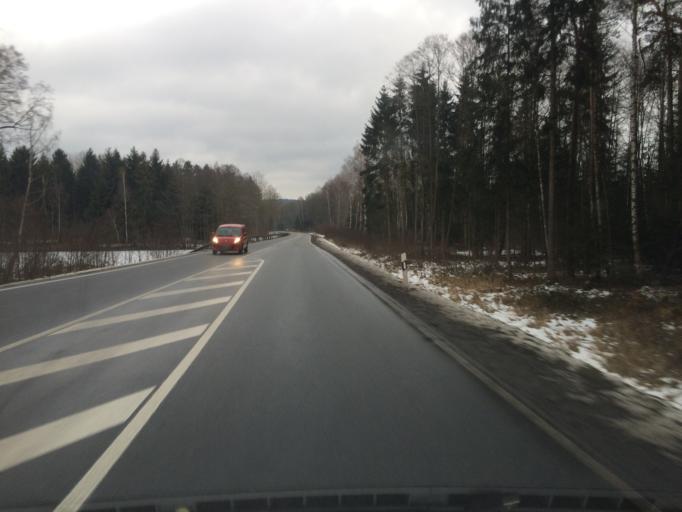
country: DE
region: Bavaria
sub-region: Upper Palatinate
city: Teublitz
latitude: 49.2217
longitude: 12.0981
